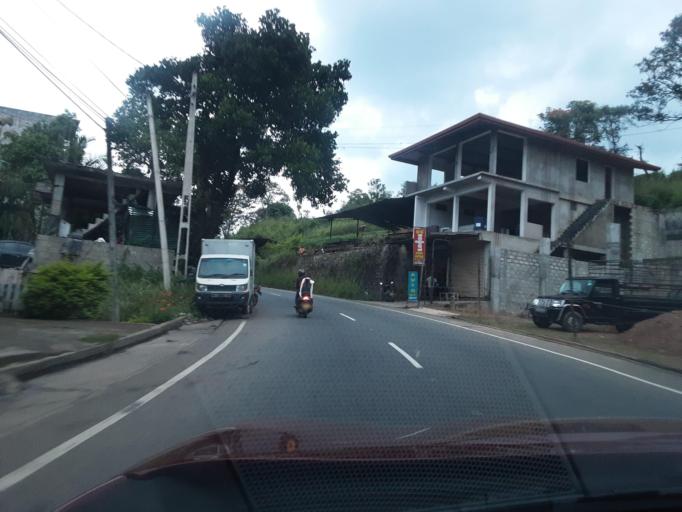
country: LK
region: Central
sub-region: Nuwara Eliya District
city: Nuwara Eliya
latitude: 6.9010
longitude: 80.9038
